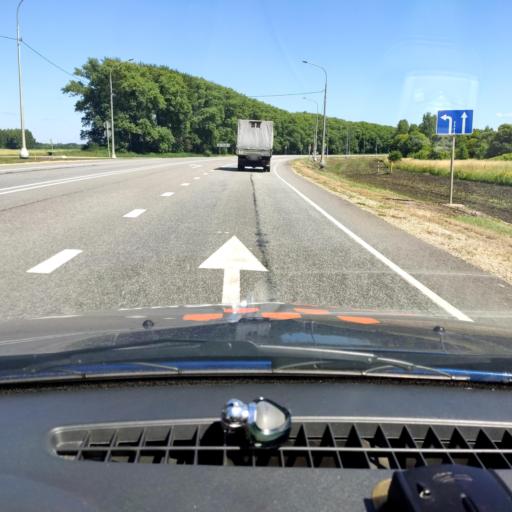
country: RU
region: Orjol
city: Pokrovskoye
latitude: 52.6420
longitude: 36.6677
